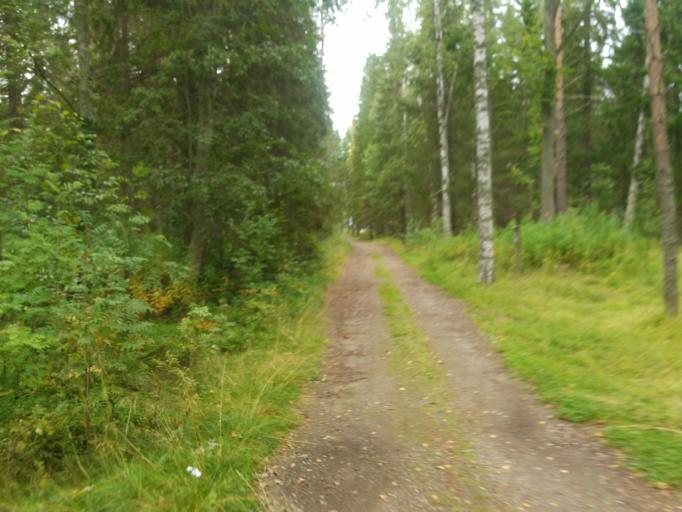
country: SE
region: Vaesterbotten
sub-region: Umea Kommun
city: Ersmark
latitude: 63.9328
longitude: 20.3851
